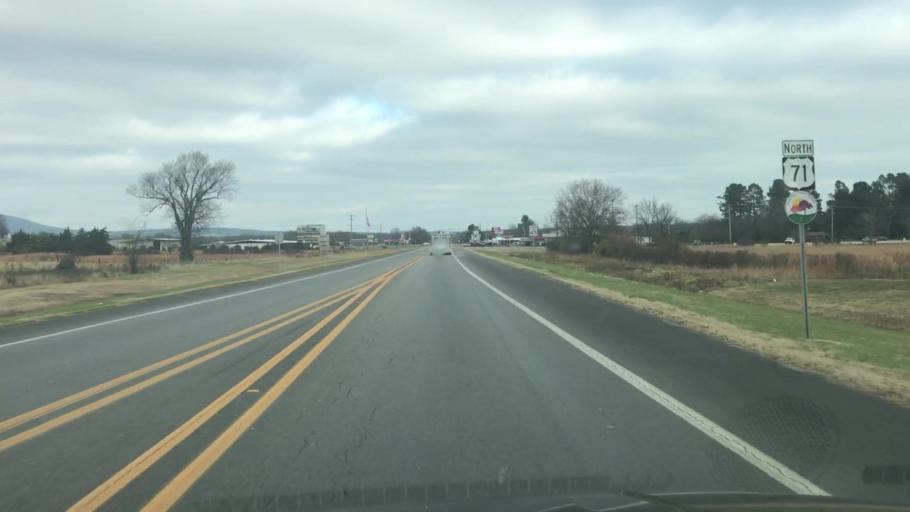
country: US
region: Arkansas
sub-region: Scott County
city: Waldron
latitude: 34.8977
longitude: -94.1075
